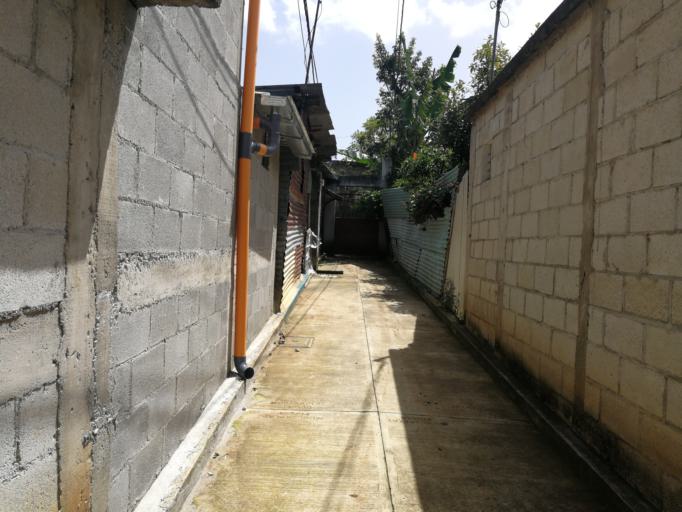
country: GT
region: Guatemala
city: Santa Catarina Pinula
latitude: 14.5458
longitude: -90.5187
